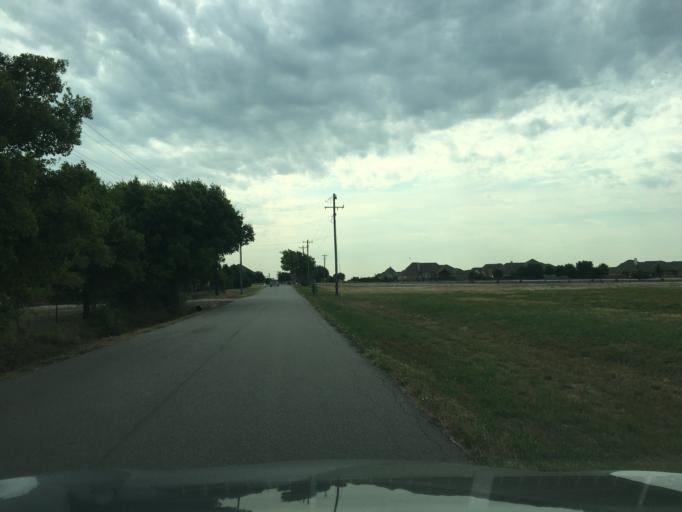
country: US
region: Texas
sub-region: Collin County
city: Parker
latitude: 33.0677
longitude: -96.6170
